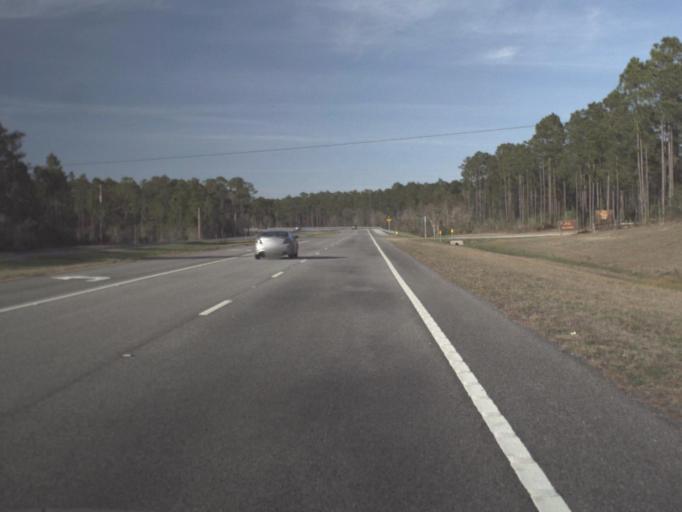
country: US
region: Florida
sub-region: Bay County
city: Laguna Beach
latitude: 30.4102
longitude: -85.8694
